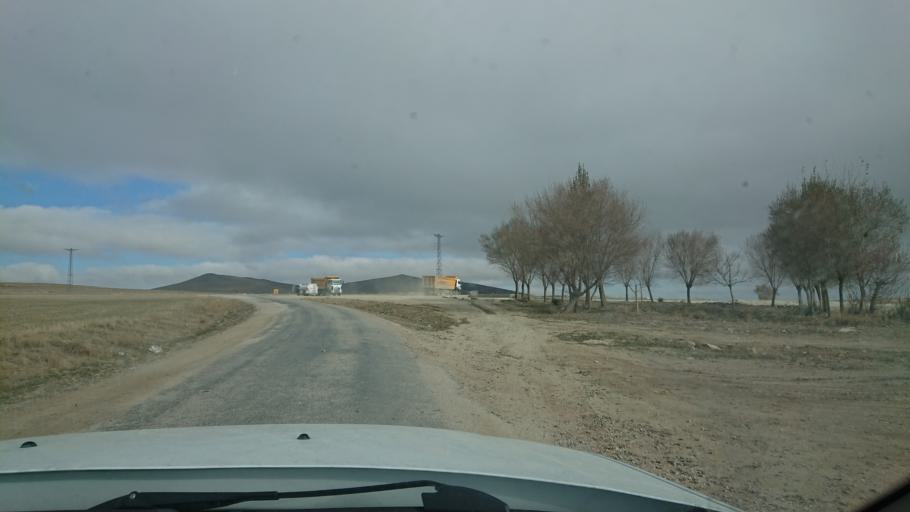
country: TR
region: Aksaray
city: Ortakoy
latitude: 38.7691
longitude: 34.0160
